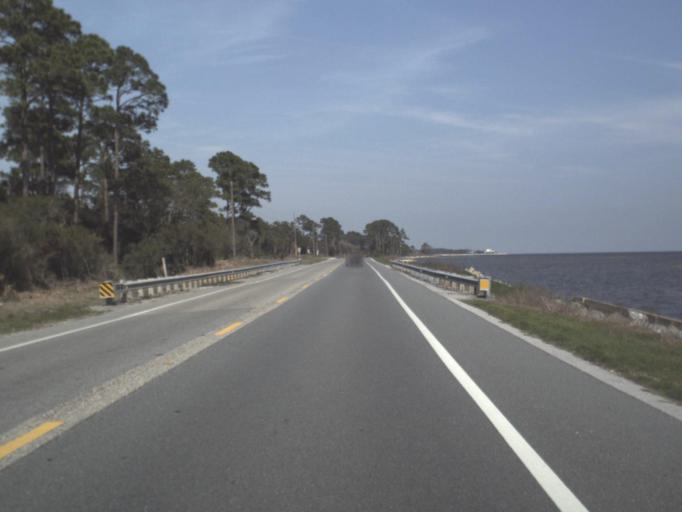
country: US
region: Florida
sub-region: Franklin County
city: Eastpoint
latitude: 29.7747
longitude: -84.7900
